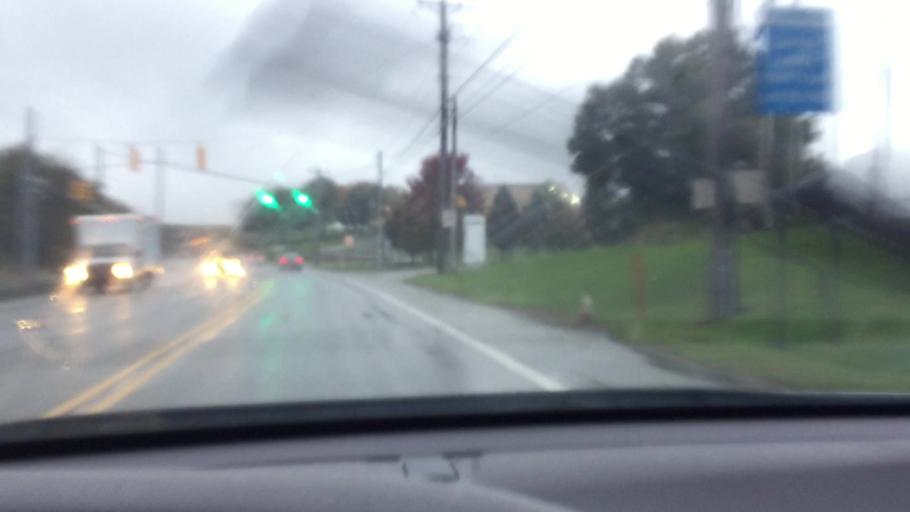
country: US
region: Pennsylvania
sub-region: Allegheny County
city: Pleasant Hills
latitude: 40.3509
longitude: -79.9419
